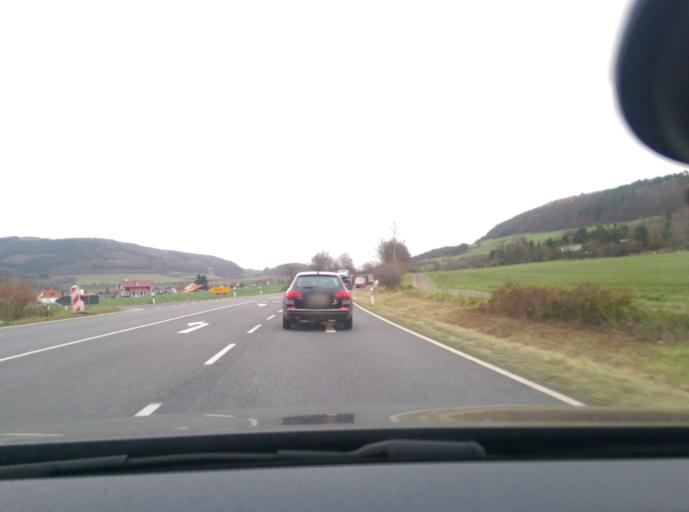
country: DE
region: Hesse
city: Witzenhausen
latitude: 51.3336
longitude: 9.8863
